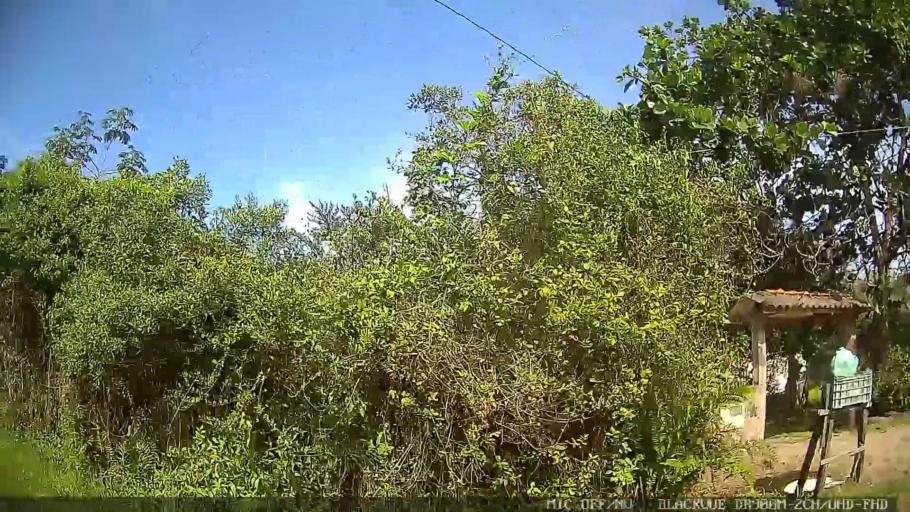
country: BR
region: Sao Paulo
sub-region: Peruibe
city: Peruibe
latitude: -24.2282
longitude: -46.9142
